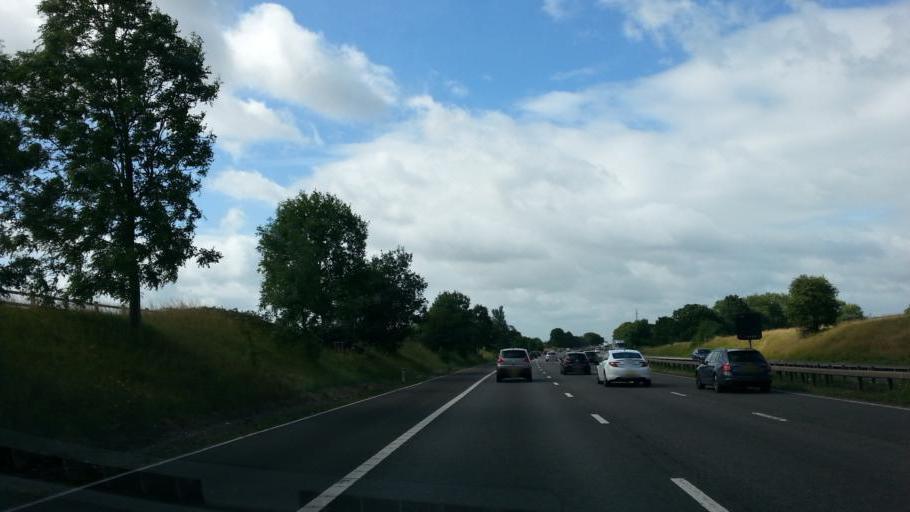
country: GB
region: England
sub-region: Warwickshire
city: Bedworth
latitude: 52.4705
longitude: -1.4053
